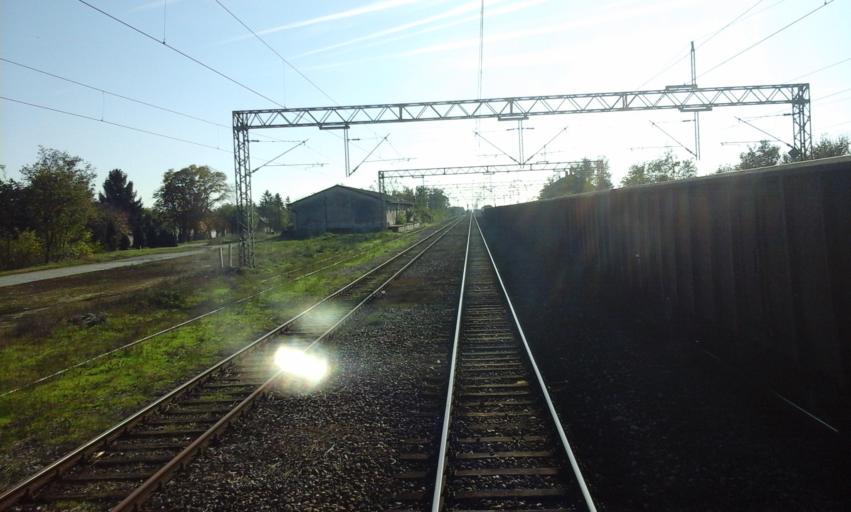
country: RS
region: Autonomna Pokrajina Vojvodina
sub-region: Severnobacki Okrug
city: Backa Topola
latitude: 45.9383
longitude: 19.6681
